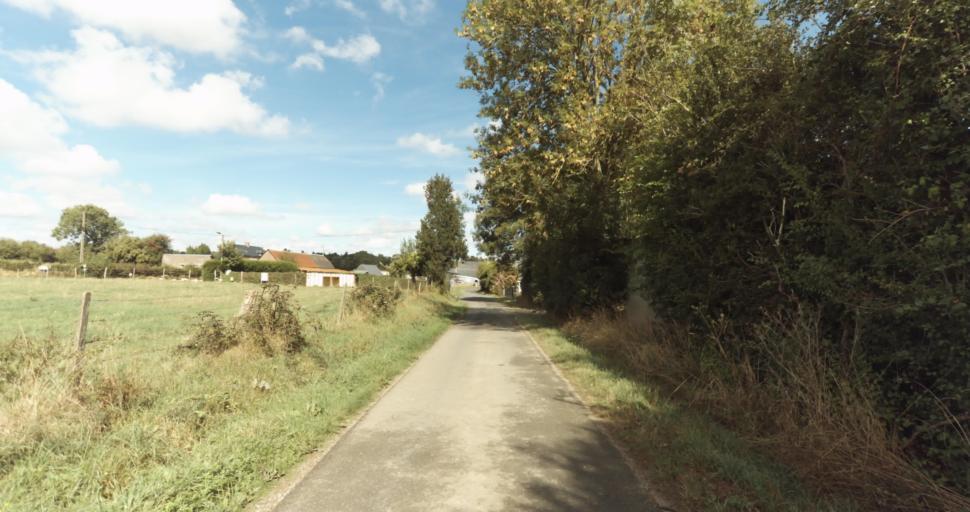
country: FR
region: Lower Normandy
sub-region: Departement du Calvados
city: Orbec
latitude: 48.9241
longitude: 0.3790
